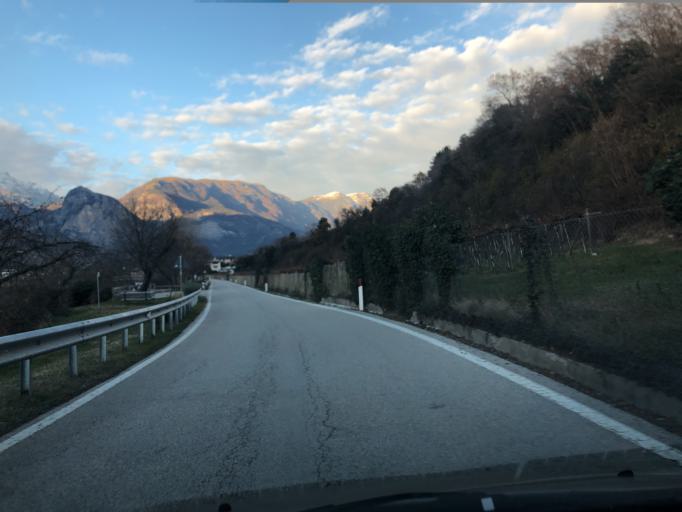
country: IT
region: Trentino-Alto Adige
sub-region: Provincia di Trento
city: Pietramurata
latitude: 46.0083
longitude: 10.9567
